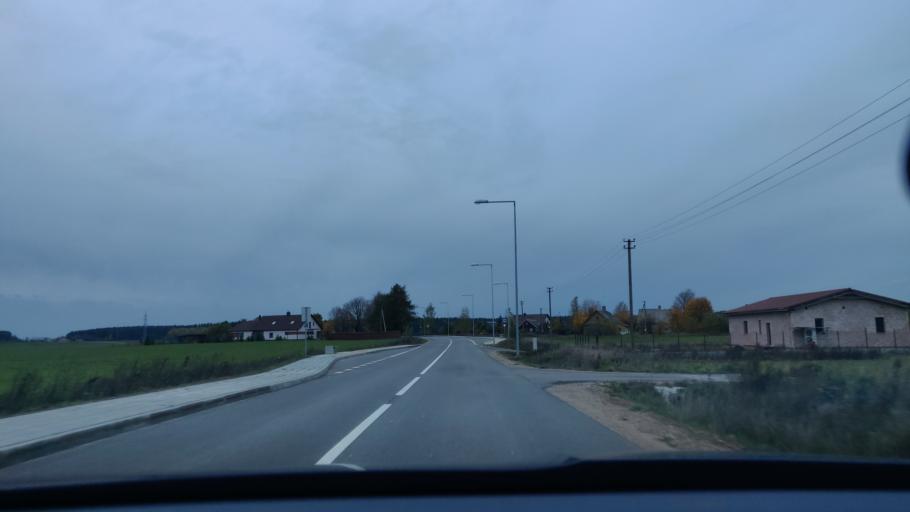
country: LT
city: Lentvaris
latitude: 54.5901
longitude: 25.0494
